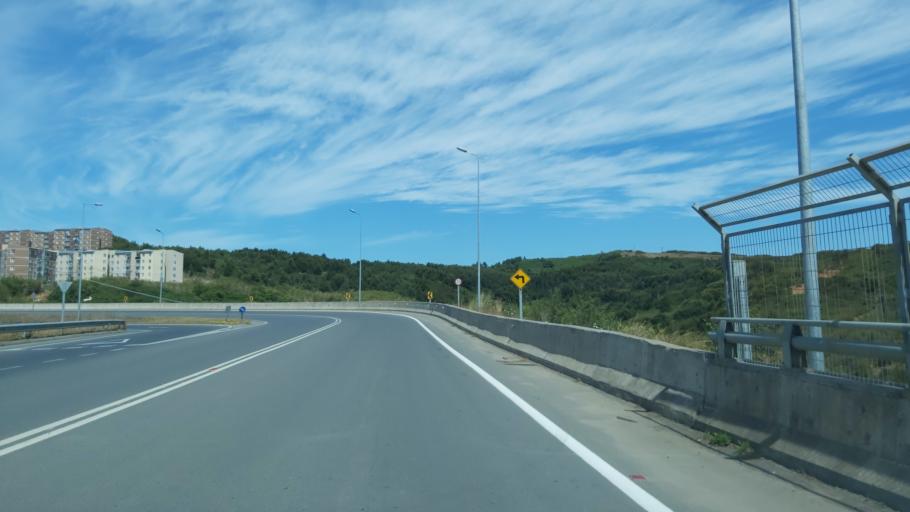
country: CL
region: Biobio
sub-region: Provincia de Concepcion
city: Coronel
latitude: -37.0238
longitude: -73.1356
